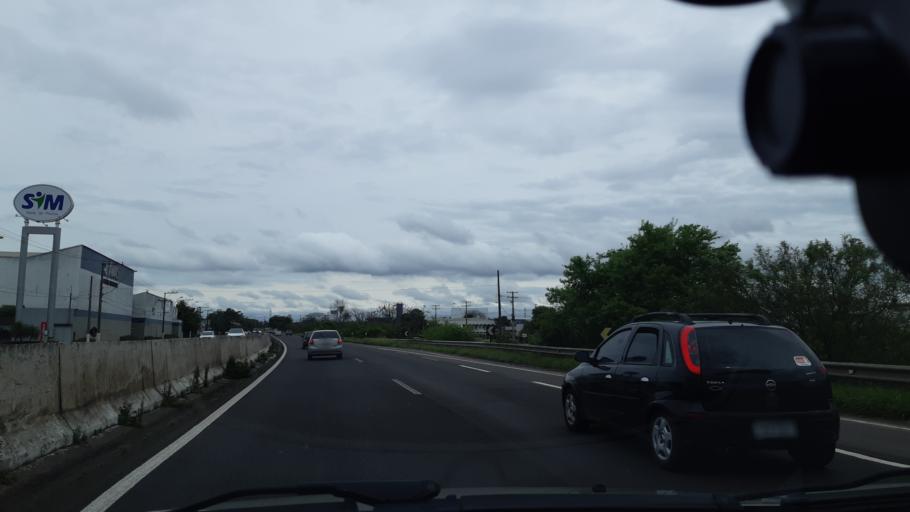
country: BR
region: Rio Grande do Sul
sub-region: Esteio
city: Esteio
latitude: -29.8603
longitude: -51.1811
